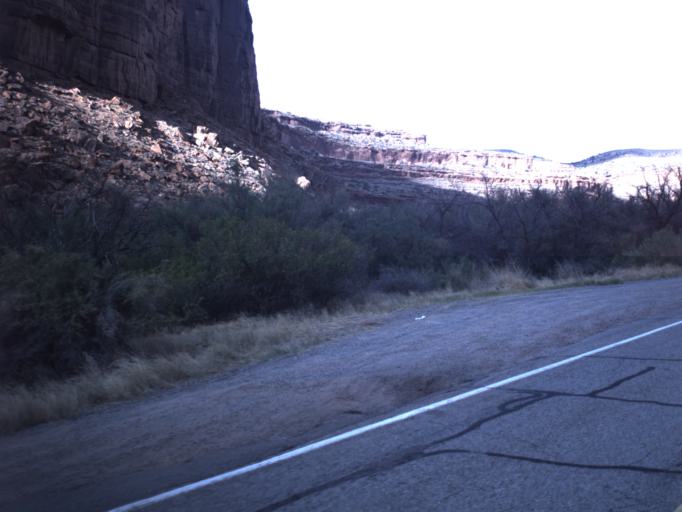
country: US
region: Utah
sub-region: Grand County
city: Moab
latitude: 38.7947
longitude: -109.3237
